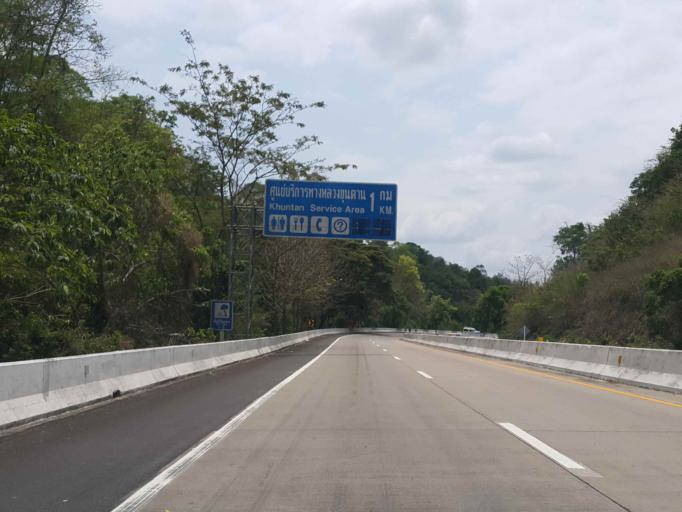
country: TH
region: Lamphun
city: Mae Tha
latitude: 18.4021
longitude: 99.2132
